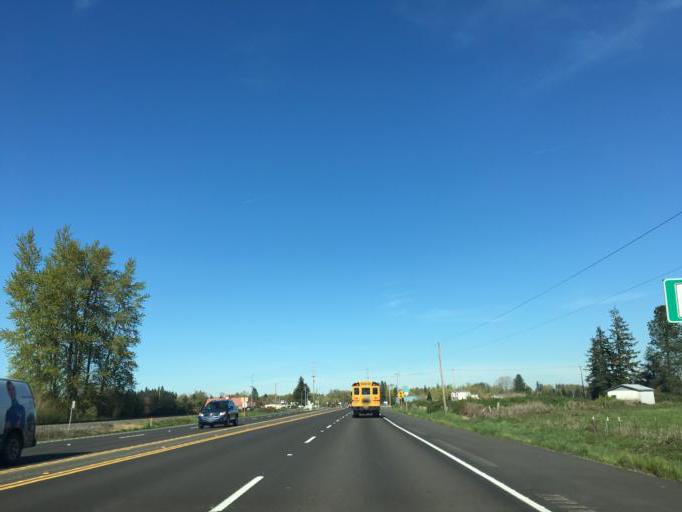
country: US
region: Oregon
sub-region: Clackamas County
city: Canby
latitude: 45.2475
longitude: -122.7260
